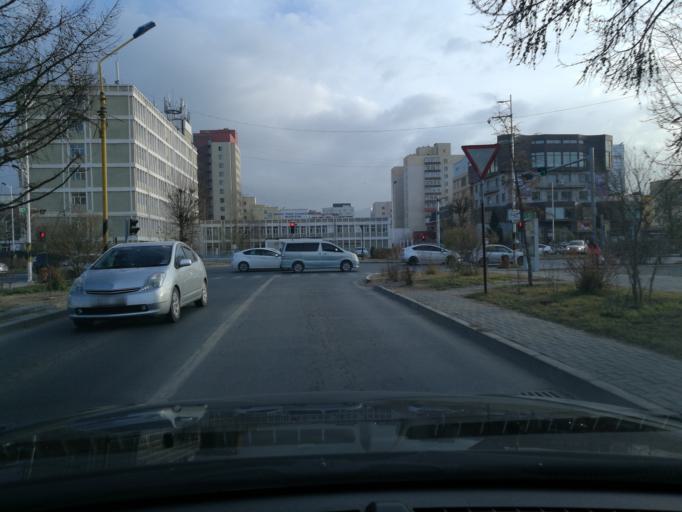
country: MN
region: Ulaanbaatar
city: Ulaanbaatar
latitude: 47.9235
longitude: 106.9277
